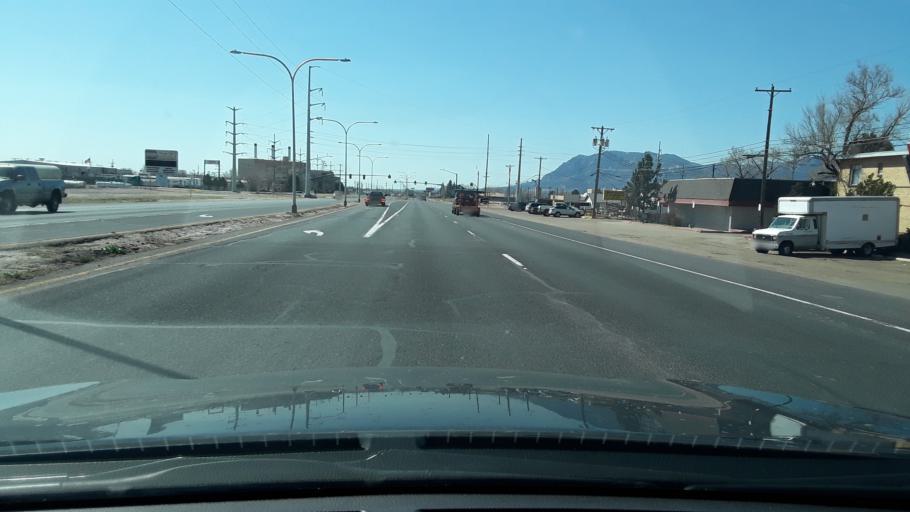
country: US
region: Colorado
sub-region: El Paso County
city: Colorado Springs
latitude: 38.8880
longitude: -104.8191
